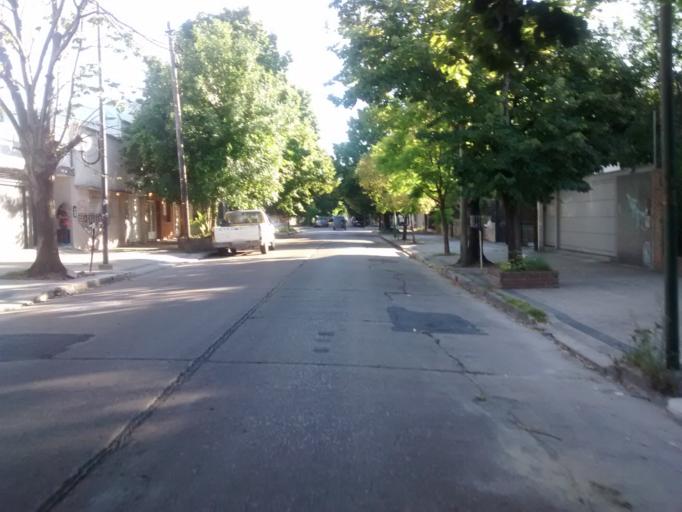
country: AR
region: Buenos Aires
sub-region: Partido de La Plata
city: La Plata
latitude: -34.9326
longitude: -57.9318
